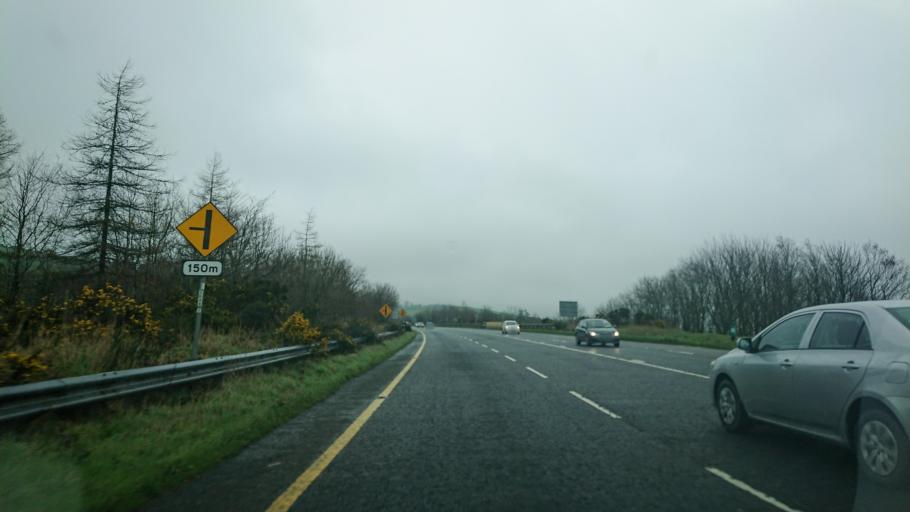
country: IE
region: Munster
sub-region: County Cork
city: Kinsale
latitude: 51.8114
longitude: -8.5394
